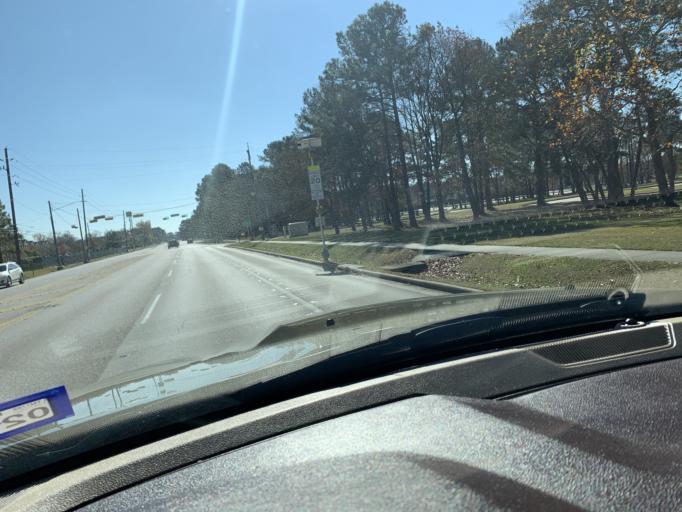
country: US
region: Texas
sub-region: Harris County
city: Spring
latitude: 30.0059
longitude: -95.4440
